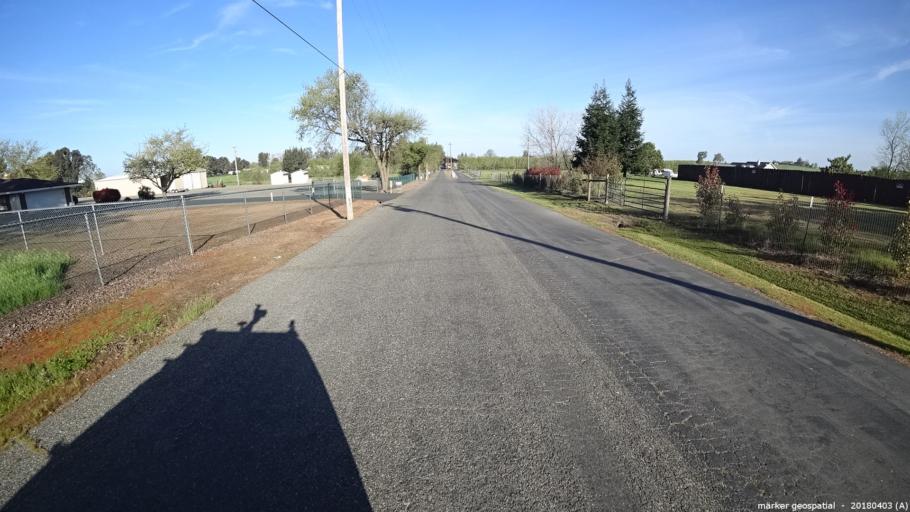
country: US
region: California
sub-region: Sacramento County
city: Wilton
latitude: 38.4452
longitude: -121.1951
